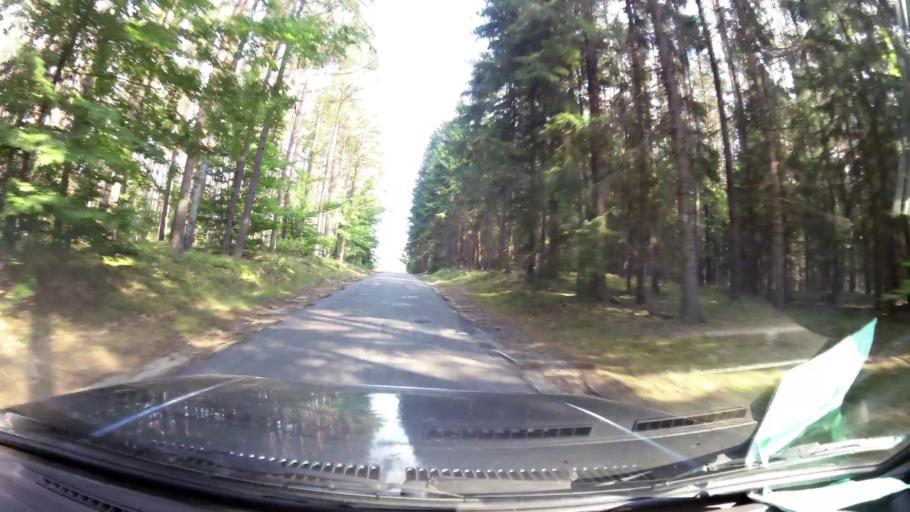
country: PL
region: West Pomeranian Voivodeship
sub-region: Powiat koszalinski
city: Bobolice
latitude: 54.0832
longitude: 16.4753
